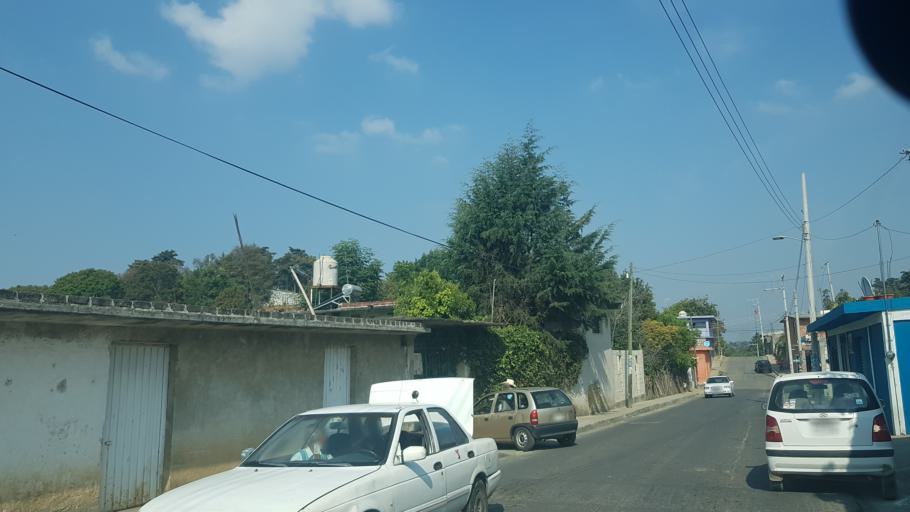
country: MX
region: Morelos
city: Hueyapan
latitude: 18.8874
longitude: -98.6872
